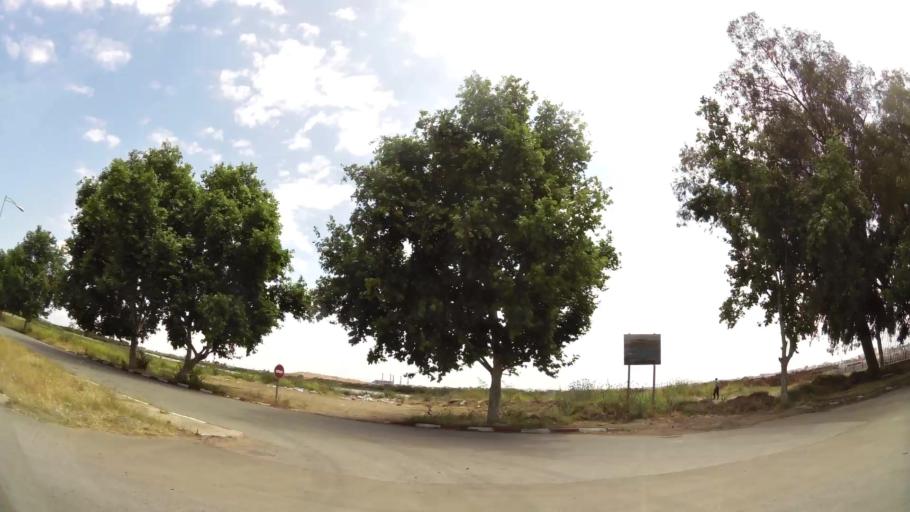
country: MA
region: Gharb-Chrarda-Beni Hssen
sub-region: Kenitra Province
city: Kenitra
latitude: 34.2750
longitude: -6.5914
